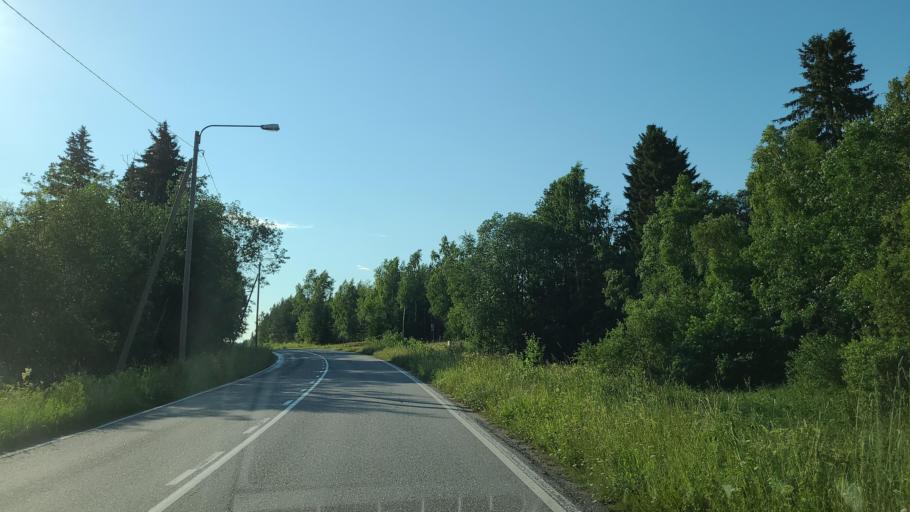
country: FI
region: Ostrobothnia
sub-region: Vaasa
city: Replot
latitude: 63.2344
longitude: 21.4038
